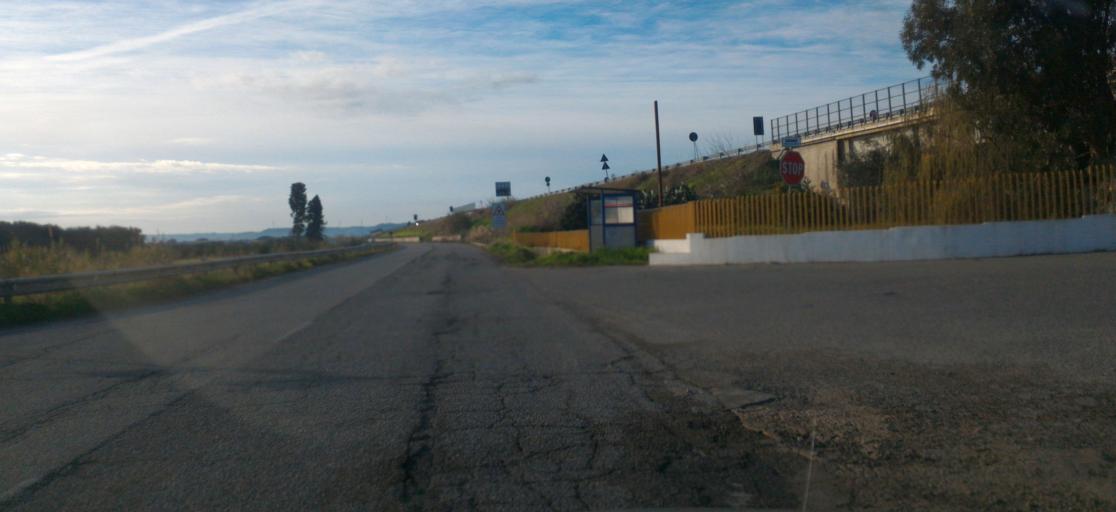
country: IT
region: Calabria
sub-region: Provincia di Crotone
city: Crotone
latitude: 39.1633
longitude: 17.0987
